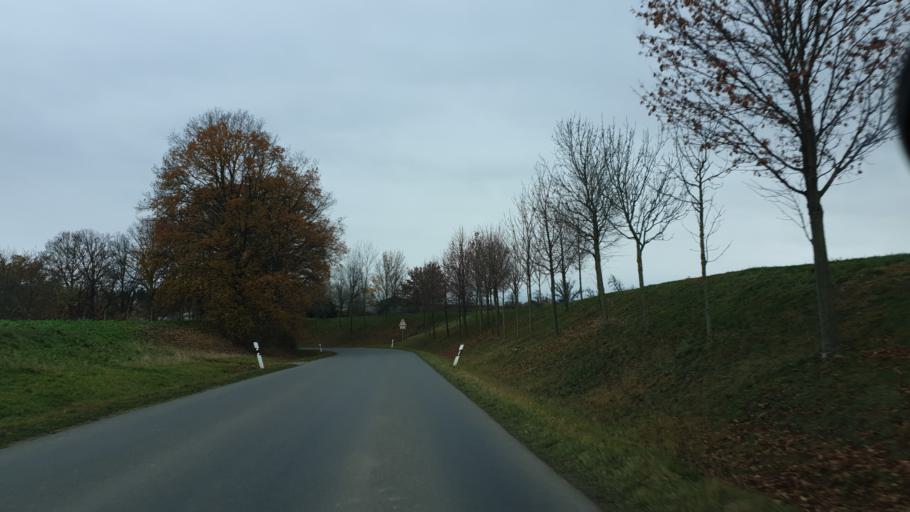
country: DE
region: Thuringia
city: Rauda
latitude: 50.9799
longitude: 11.9405
